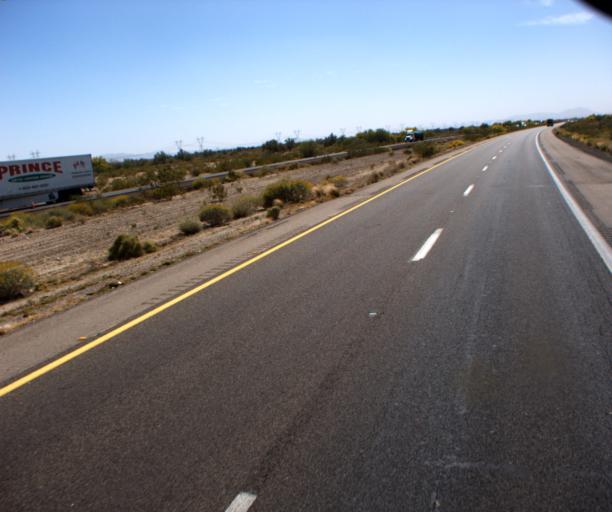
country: US
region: Arizona
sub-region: Maricopa County
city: Gila Bend
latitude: 33.0194
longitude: -112.6506
